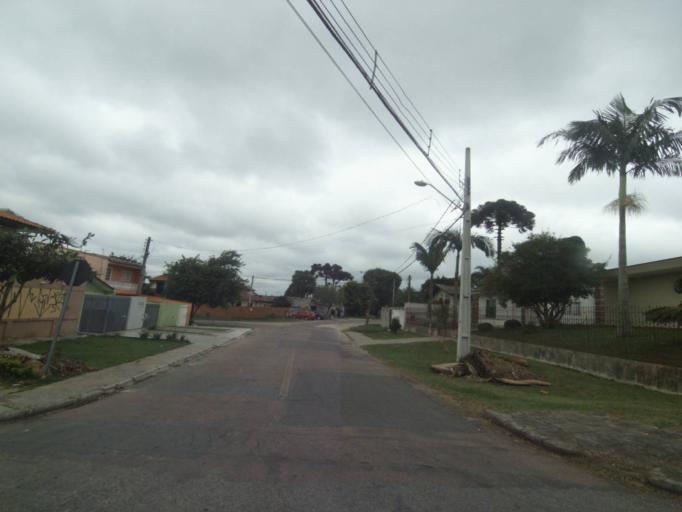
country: BR
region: Parana
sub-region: Sao Jose Dos Pinhais
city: Sao Jose dos Pinhais
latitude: -25.5420
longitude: -49.2792
